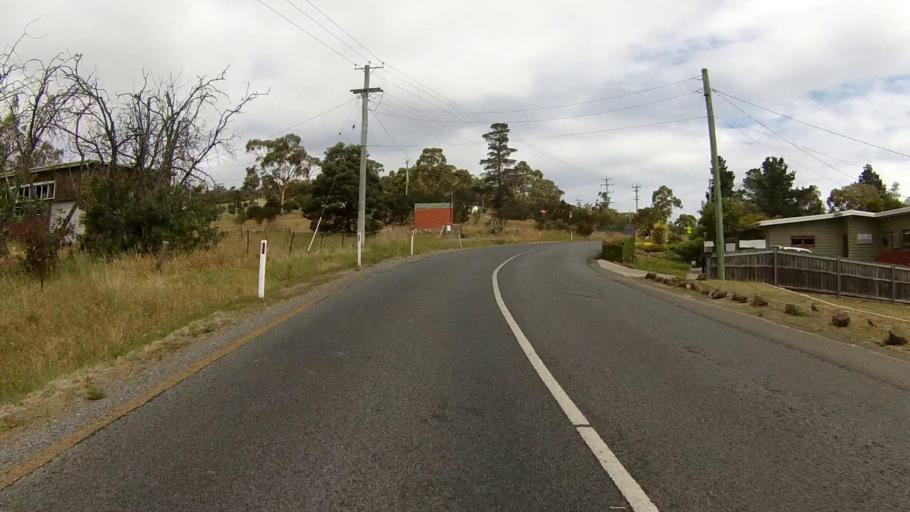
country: AU
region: Tasmania
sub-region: Clarence
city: Cambridge
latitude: -42.8502
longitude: 147.4212
